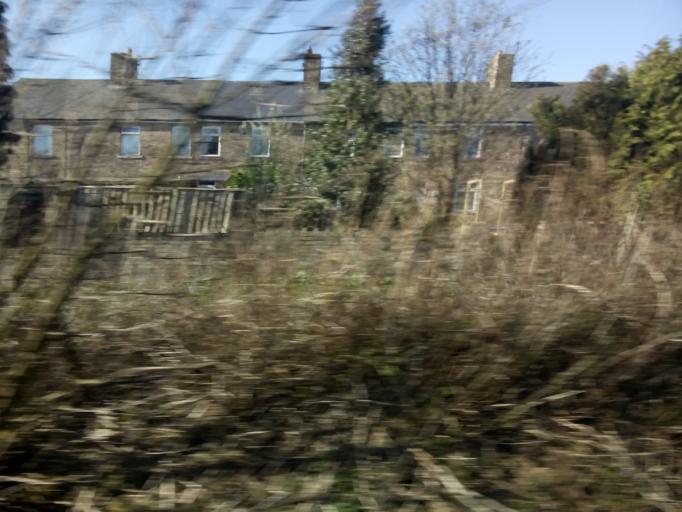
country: GB
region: England
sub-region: Northumberland
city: East Chevington
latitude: 55.2447
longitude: -1.6234
